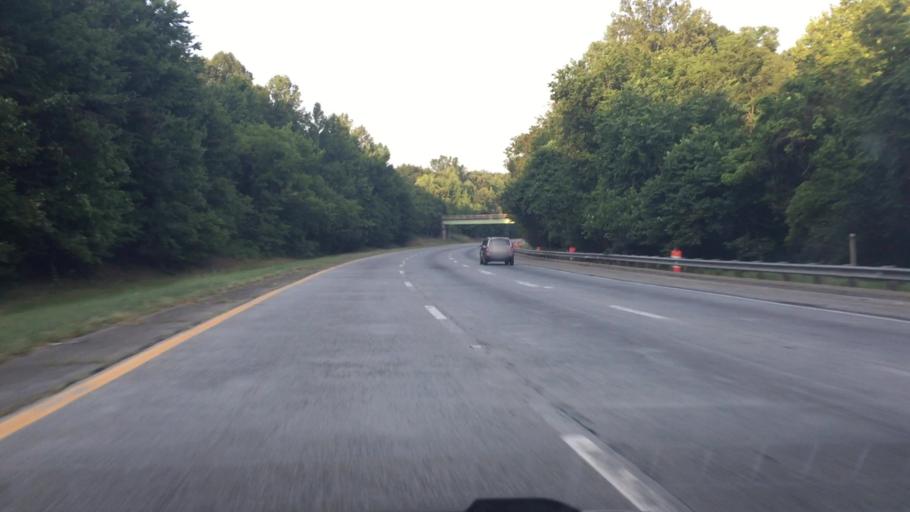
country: US
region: North Carolina
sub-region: Davidson County
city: Thomasville
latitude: 35.8370
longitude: -80.1337
